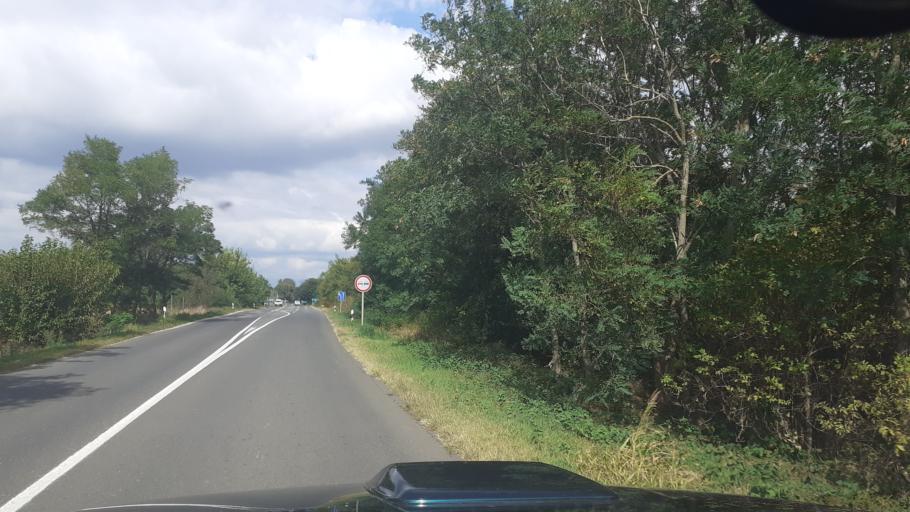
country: HU
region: Bacs-Kiskun
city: Apostag
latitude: 46.8829
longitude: 18.9774
